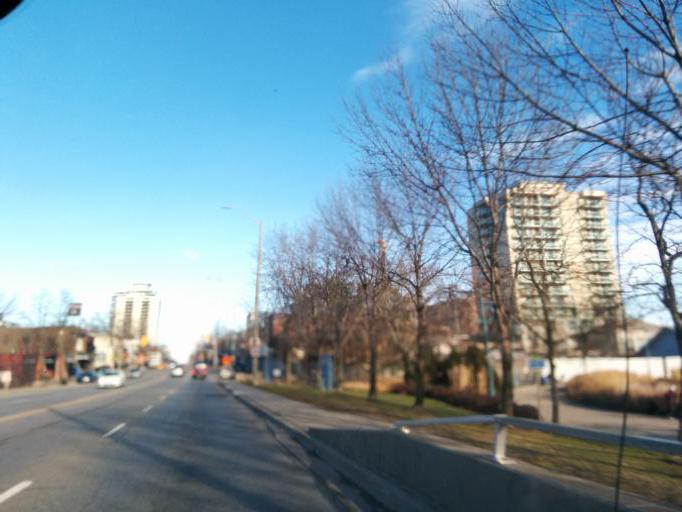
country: CA
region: Ontario
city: Mississauga
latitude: 43.5512
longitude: -79.5862
